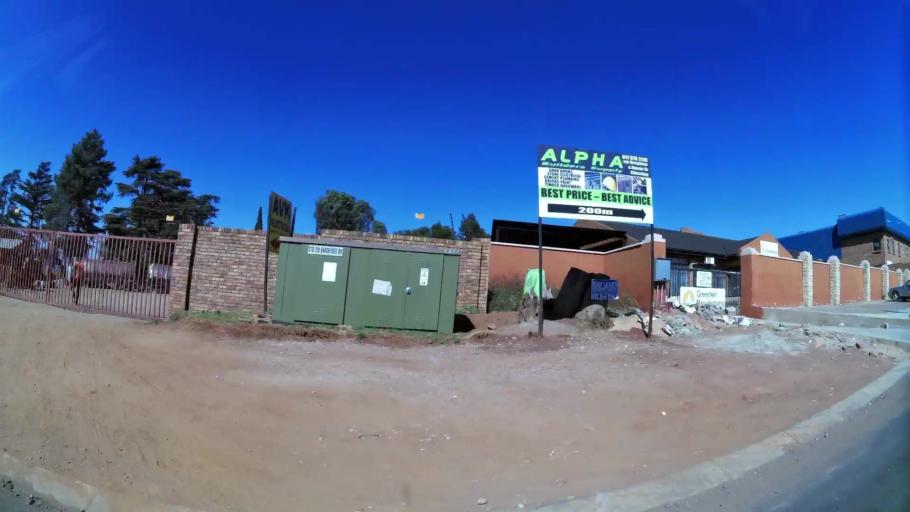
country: ZA
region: Gauteng
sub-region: City of Johannesburg Metropolitan Municipality
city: Modderfontein
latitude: -26.0747
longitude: 28.1898
